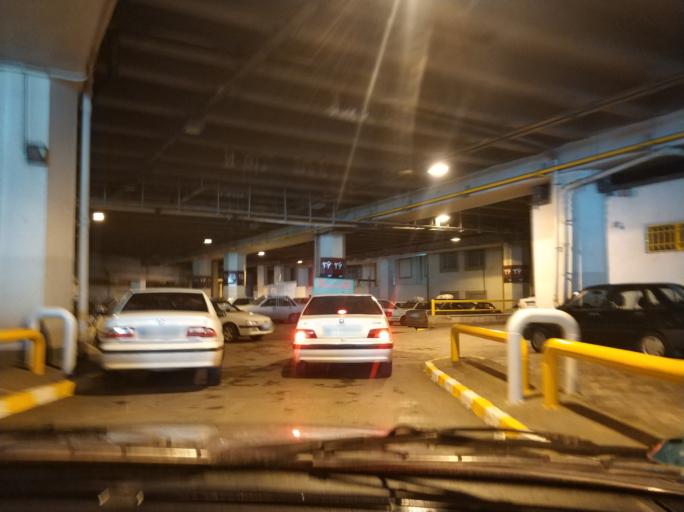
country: IR
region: Razavi Khorasan
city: Mashhad
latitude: 36.2864
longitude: 59.6186
